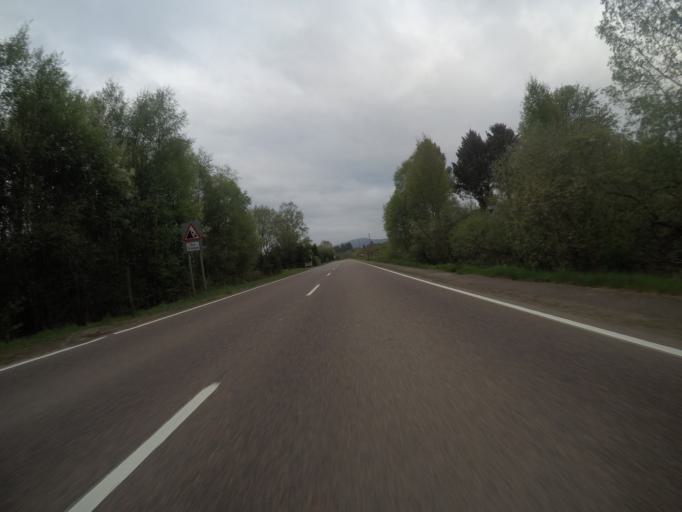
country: GB
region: Scotland
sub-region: Highland
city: Spean Bridge
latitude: 56.8902
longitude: -4.8654
